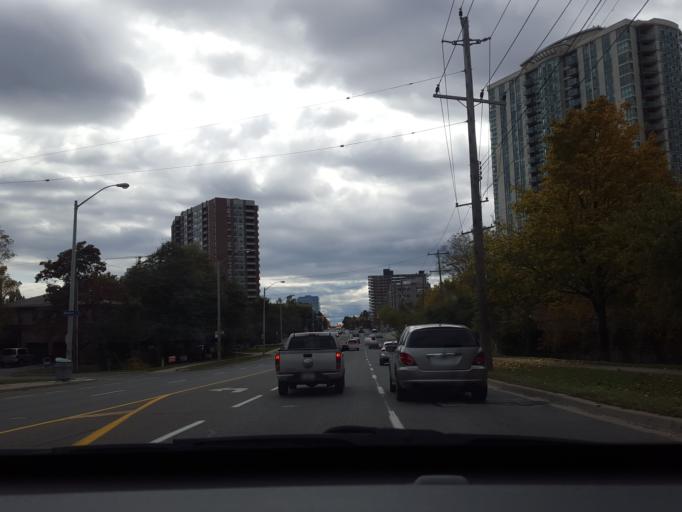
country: CA
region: Ontario
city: Scarborough
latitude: 43.7876
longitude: -79.2904
